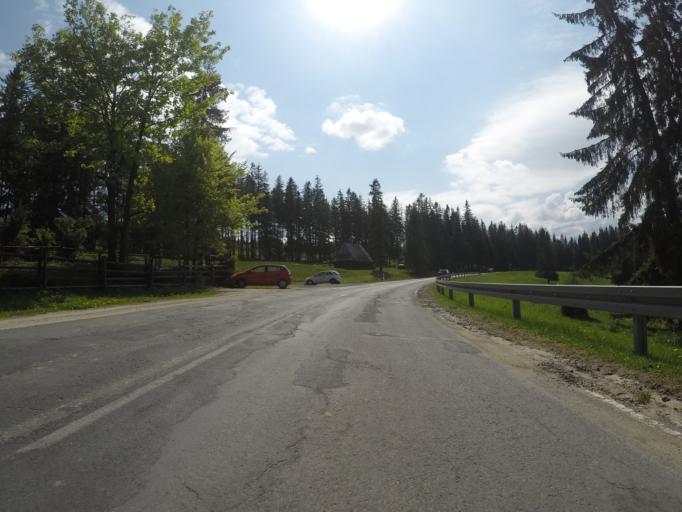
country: PL
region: Lesser Poland Voivodeship
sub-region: Powiat tatrzanski
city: Bukowina Tatrzanska
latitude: 49.3054
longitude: 20.1143
